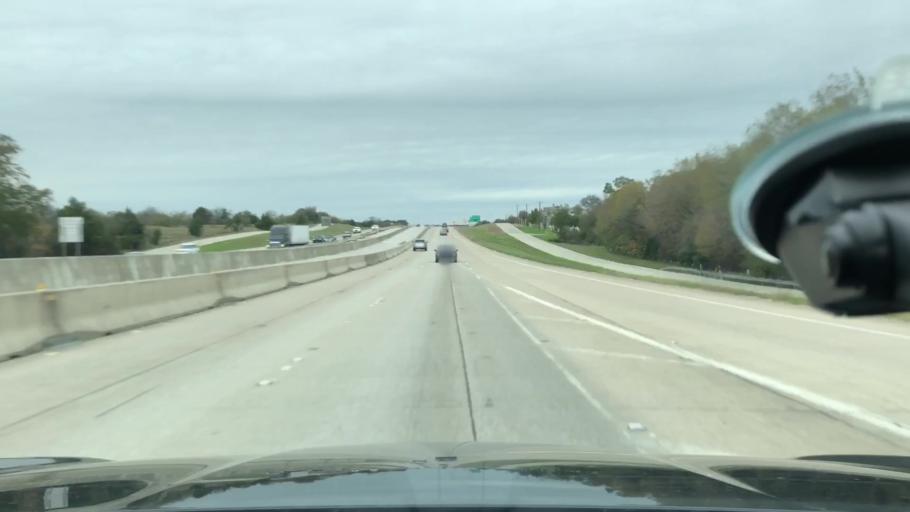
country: US
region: Texas
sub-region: Ellis County
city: Waxahachie
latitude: 32.3869
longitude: -96.8681
